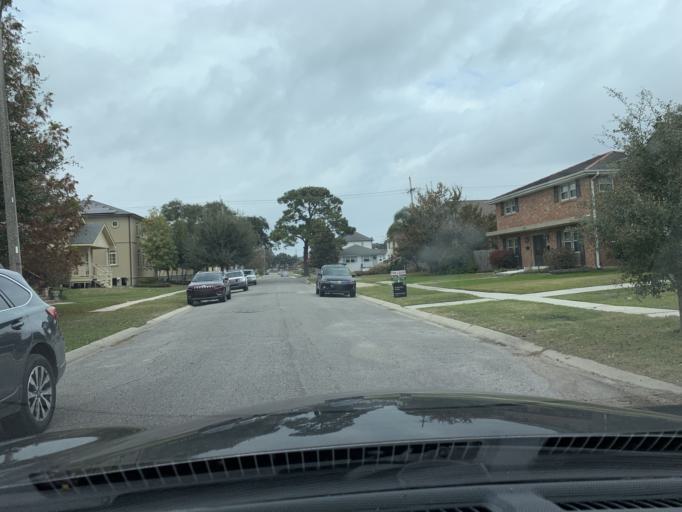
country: US
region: Louisiana
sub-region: Jefferson Parish
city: Metairie
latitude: 30.0165
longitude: -90.1023
